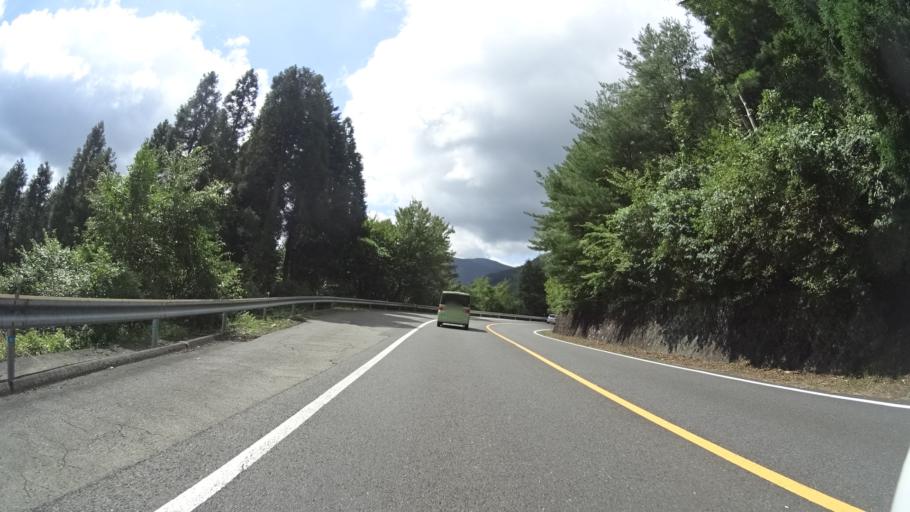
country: JP
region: Oita
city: Tsukawaki
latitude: 33.2065
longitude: 131.2911
